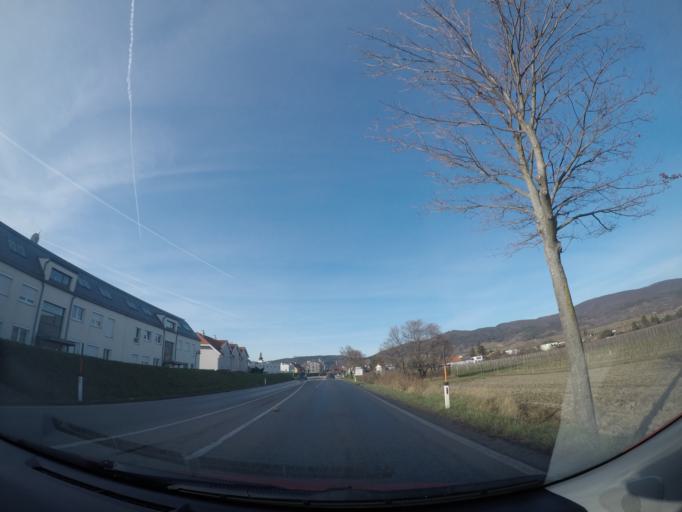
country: AT
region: Lower Austria
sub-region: Politischer Bezirk Baden
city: Pfaffstatten
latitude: 48.0165
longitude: 16.2705
